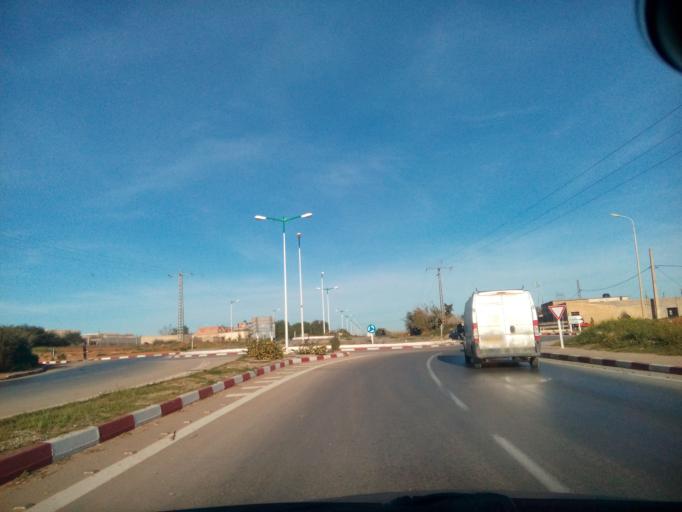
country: DZ
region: Mostaganem
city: Mostaganem
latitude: 35.8693
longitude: 0.1506
